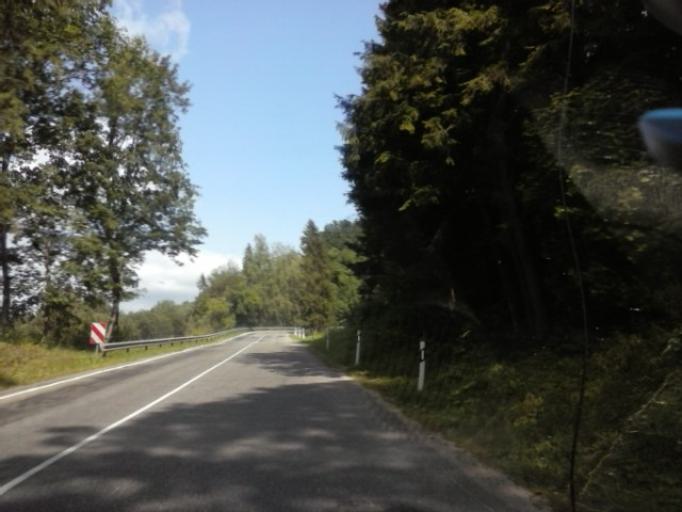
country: LV
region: Sigulda
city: Sigulda
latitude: 57.1717
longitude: 24.8430
